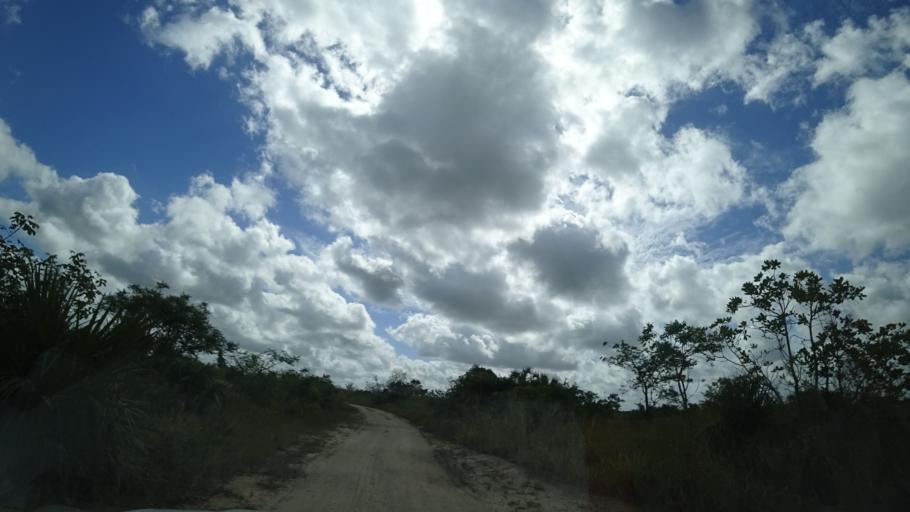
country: MZ
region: Sofala
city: Dondo
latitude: -19.3859
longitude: 34.5924
